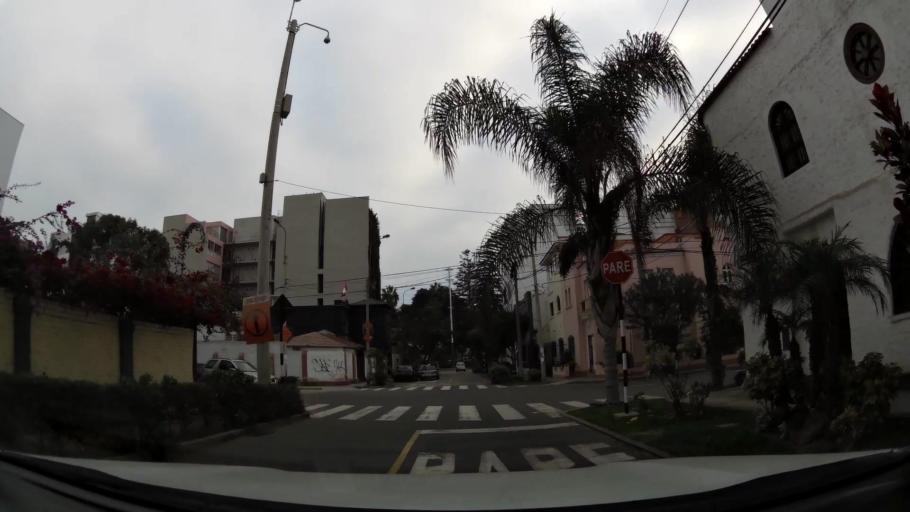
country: PE
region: Lima
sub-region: Lima
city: Surco
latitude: -12.1360
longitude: -77.0218
